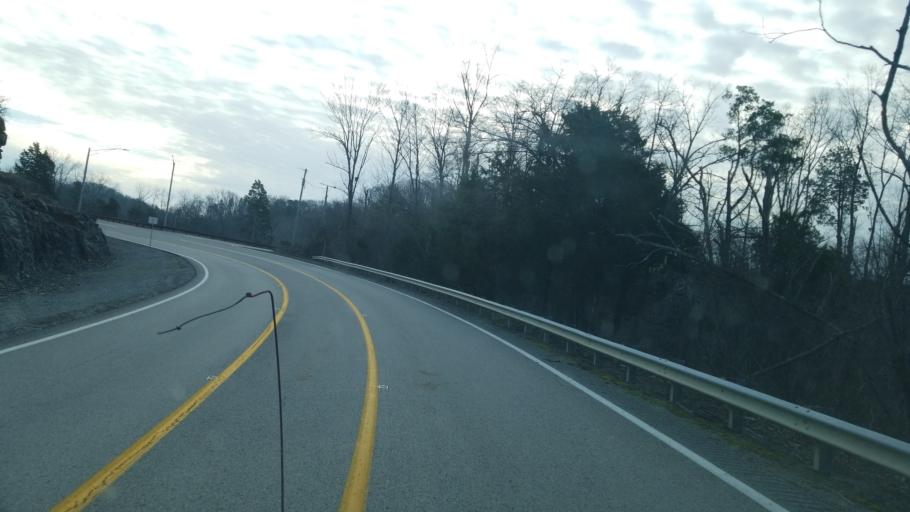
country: US
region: Kentucky
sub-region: Russell County
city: Jamestown
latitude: 36.8707
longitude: -85.1299
